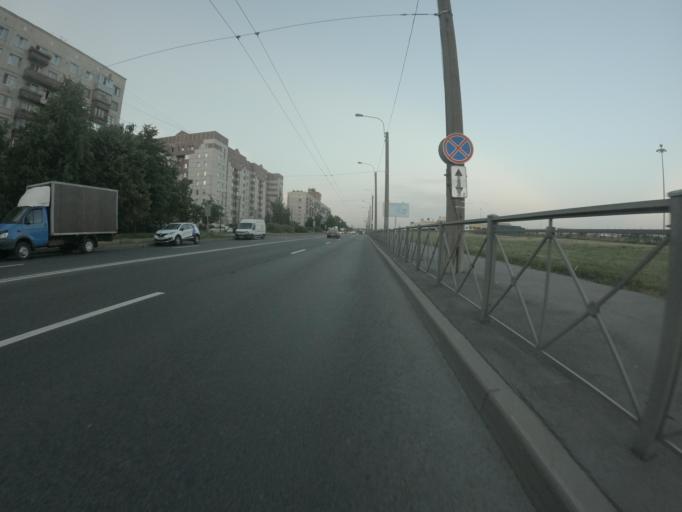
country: RU
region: St.-Petersburg
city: Krasnogvargeisky
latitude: 59.9358
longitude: 30.4925
